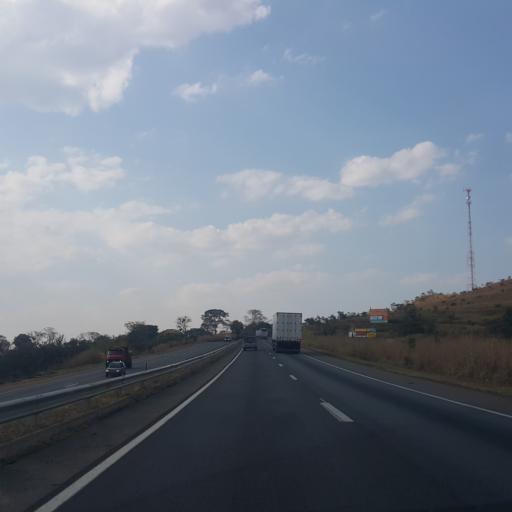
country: BR
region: Goias
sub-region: Abadiania
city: Abadiania
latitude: -16.1020
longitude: -48.5234
